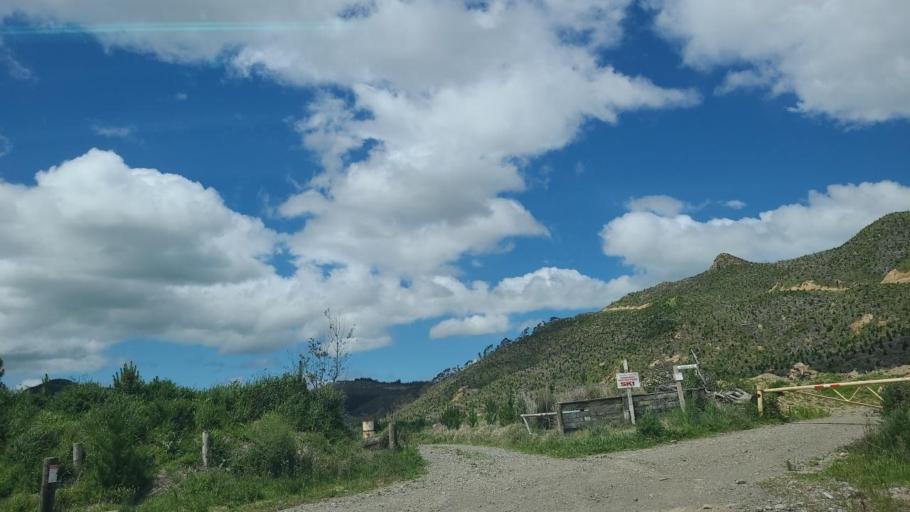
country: NZ
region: Hawke's Bay
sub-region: Napier City
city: Napier
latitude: -39.2223
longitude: 176.7841
